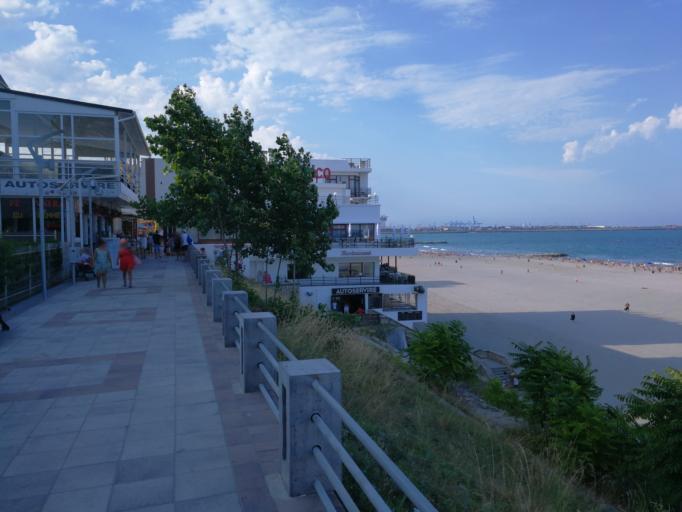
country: RO
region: Constanta
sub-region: Oras Eforie
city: Eforie Nord
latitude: 44.0700
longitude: 28.6384
